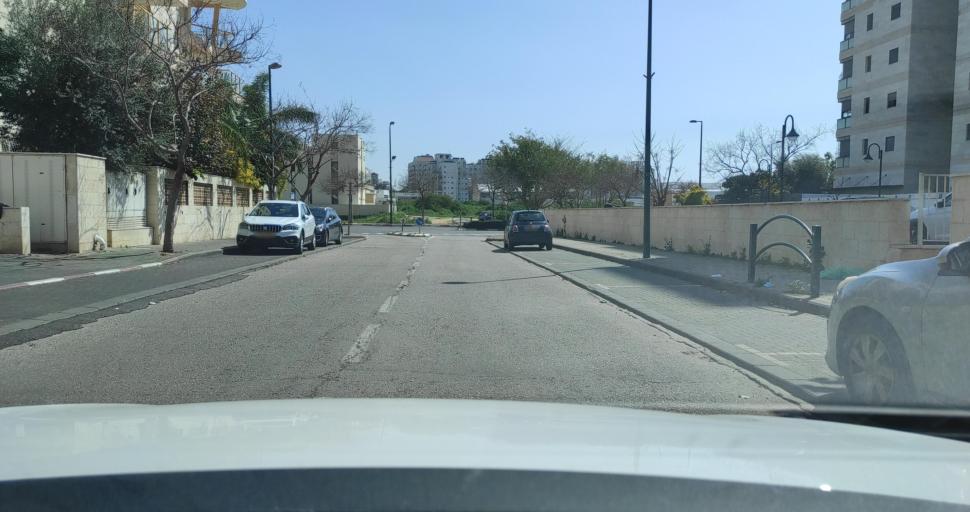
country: IL
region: Central District
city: Nordiyya
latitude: 32.3070
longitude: 34.8714
